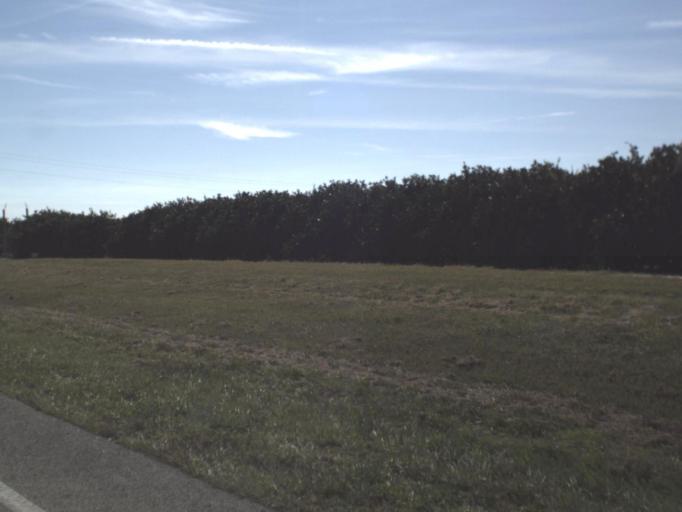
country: US
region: Florida
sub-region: Highlands County
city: Placid Lakes
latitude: 27.1394
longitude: -81.3290
